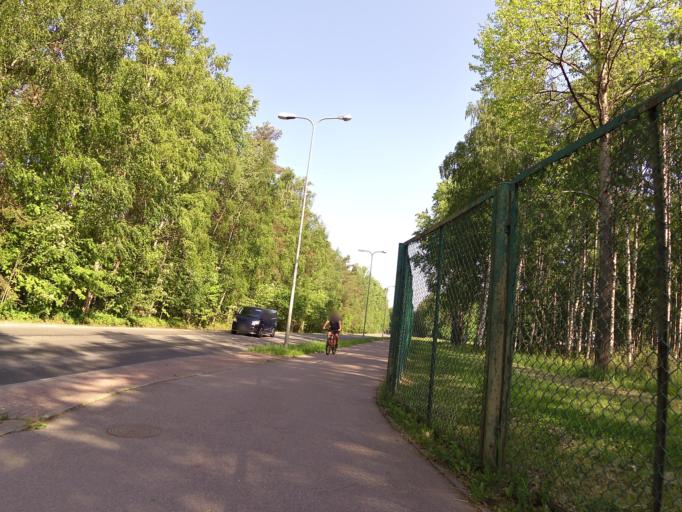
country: EE
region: Harju
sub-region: Saue vald
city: Laagri
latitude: 59.4350
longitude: 24.6286
